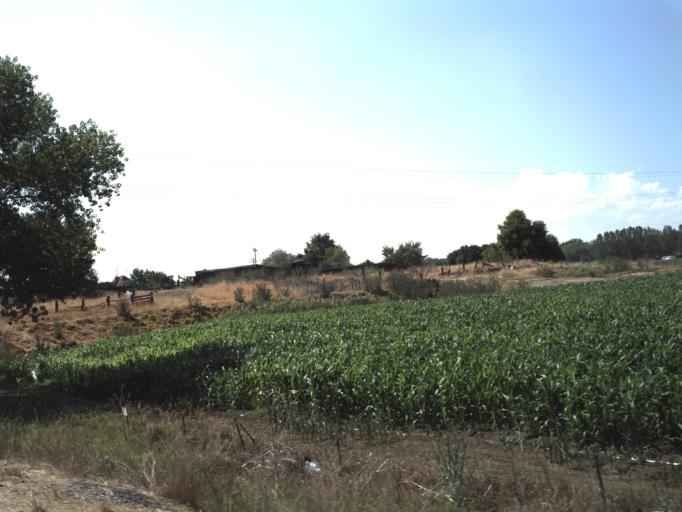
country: US
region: Utah
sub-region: Weber County
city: Marriott-Slaterville
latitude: 41.2447
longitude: -112.0408
